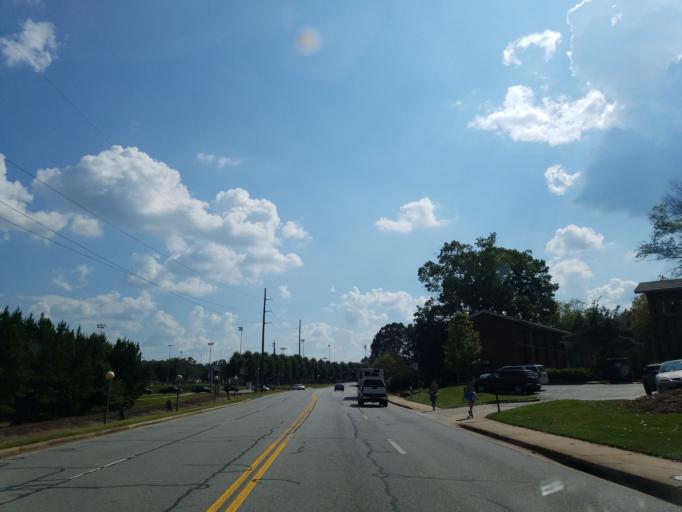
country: US
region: Georgia
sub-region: Clarke County
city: Athens
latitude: 33.9369
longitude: -83.3734
